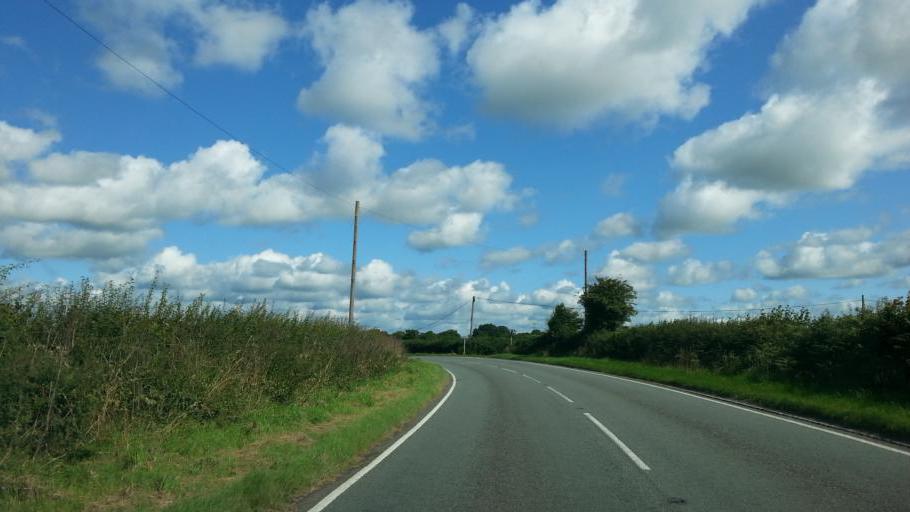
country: GB
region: England
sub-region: Staffordshire
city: Uttoxeter
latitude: 52.8606
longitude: -1.8924
